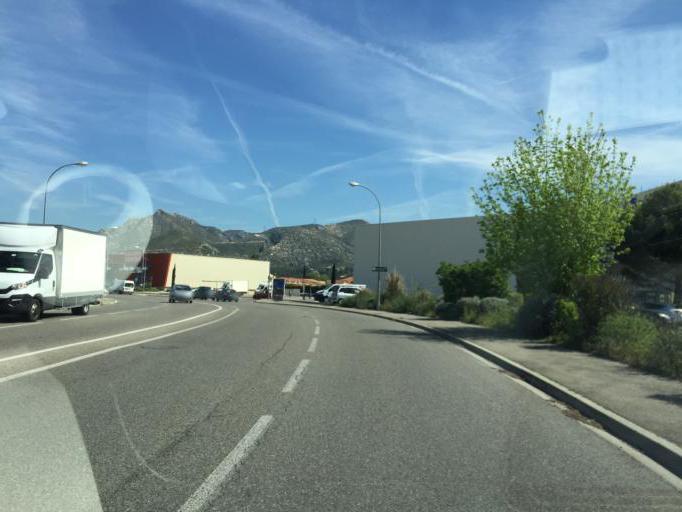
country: FR
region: Provence-Alpes-Cote d'Azur
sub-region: Departement des Bouches-du-Rhone
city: Aubagne
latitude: 43.2965
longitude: 5.5962
